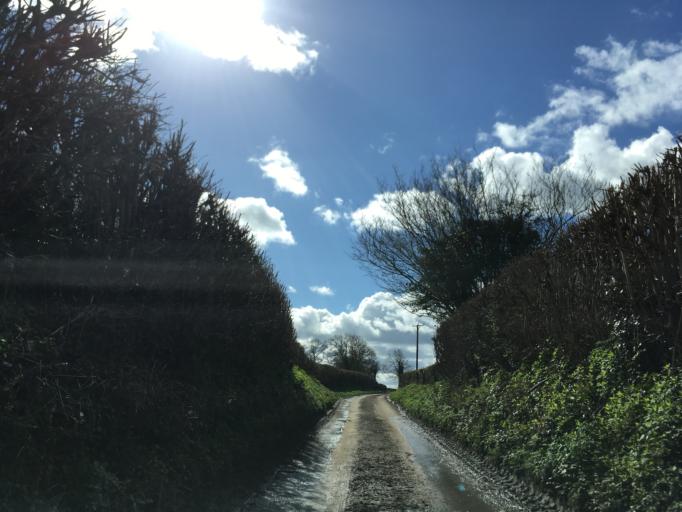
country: GB
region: England
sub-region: South Gloucestershire
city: Horton
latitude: 51.5791
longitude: -2.3384
